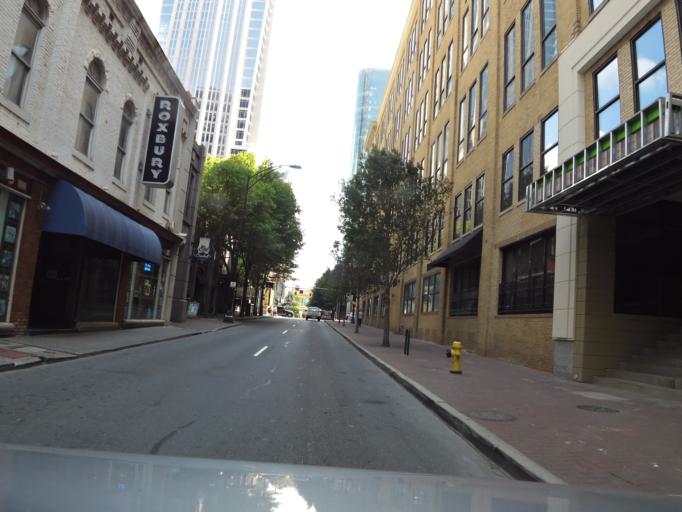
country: US
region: North Carolina
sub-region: Mecklenburg County
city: Charlotte
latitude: 35.2287
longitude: -80.8427
